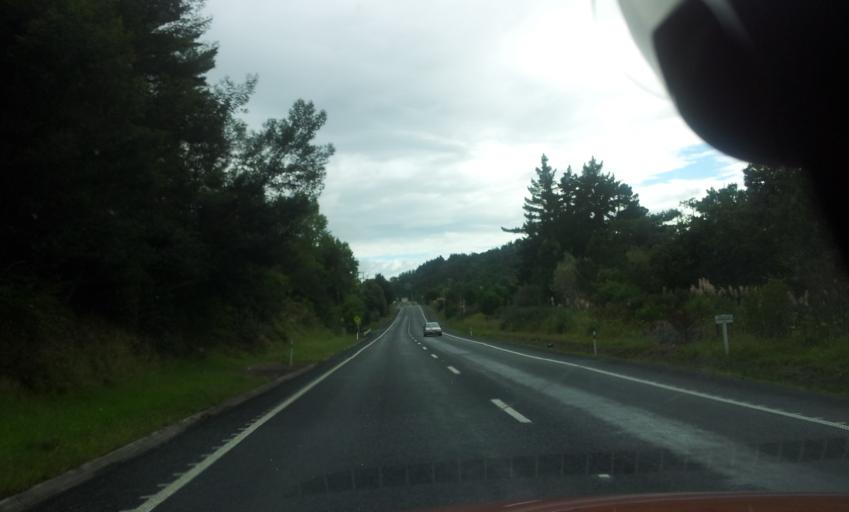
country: NZ
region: Auckland
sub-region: Auckland
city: Wellsford
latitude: -36.2624
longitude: 174.5097
